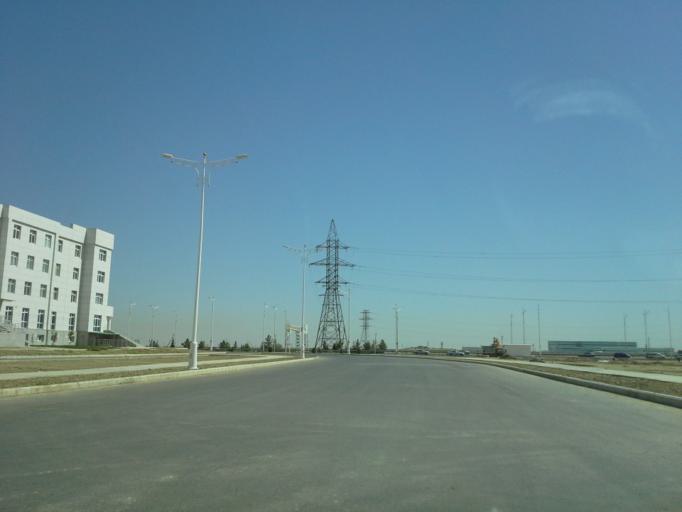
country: TM
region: Ahal
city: Ashgabat
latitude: 37.9792
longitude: 58.3360
